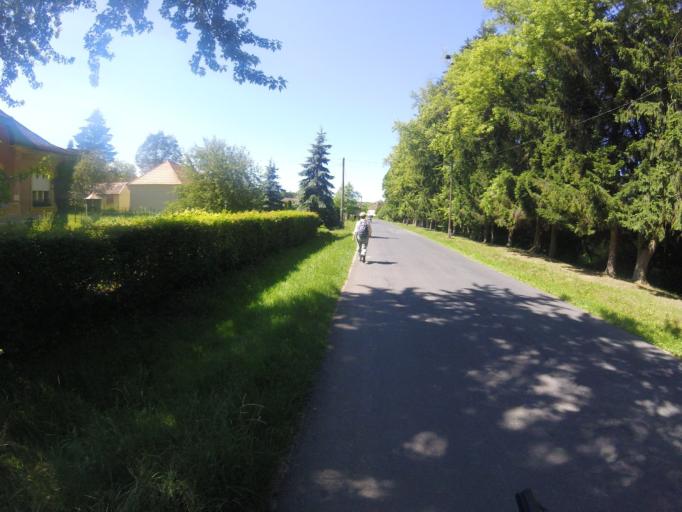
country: HU
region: Zala
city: Zalalovo
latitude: 46.8392
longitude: 16.4997
